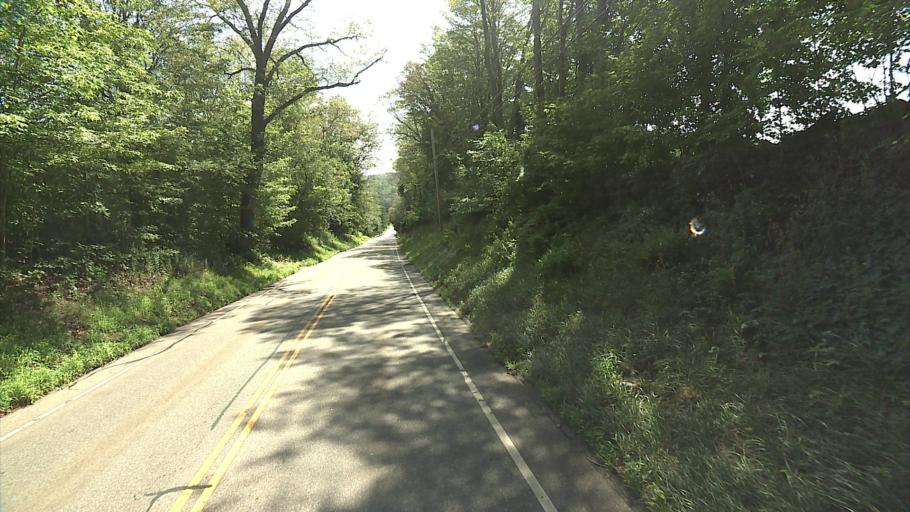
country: US
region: Connecticut
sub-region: Windham County
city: Windham
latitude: 41.6976
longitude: -72.1166
